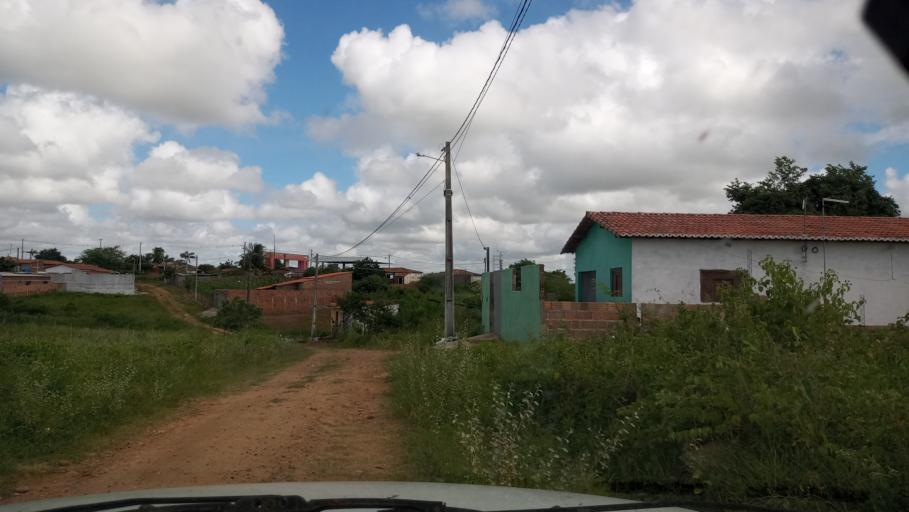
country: BR
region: Rio Grande do Norte
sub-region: Brejinho
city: Brejinho
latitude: -6.1459
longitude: -35.4309
